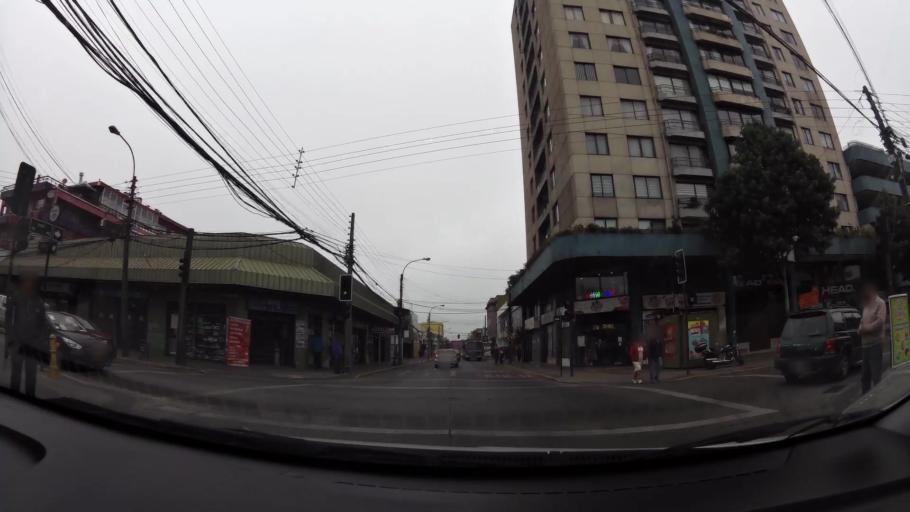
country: CL
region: Biobio
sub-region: Provincia de Concepcion
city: Concepcion
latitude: -36.8268
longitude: -73.0543
